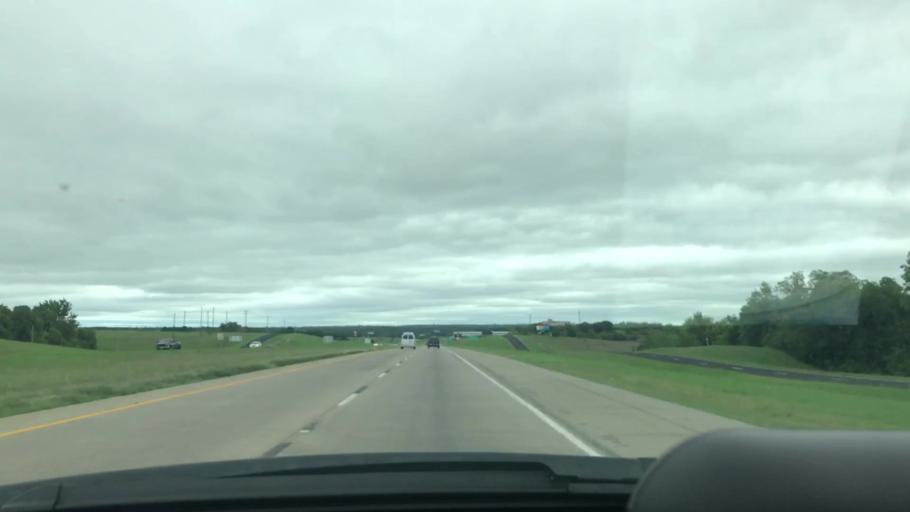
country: US
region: Texas
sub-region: Grayson County
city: Sherman
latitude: 33.6966
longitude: -96.5973
